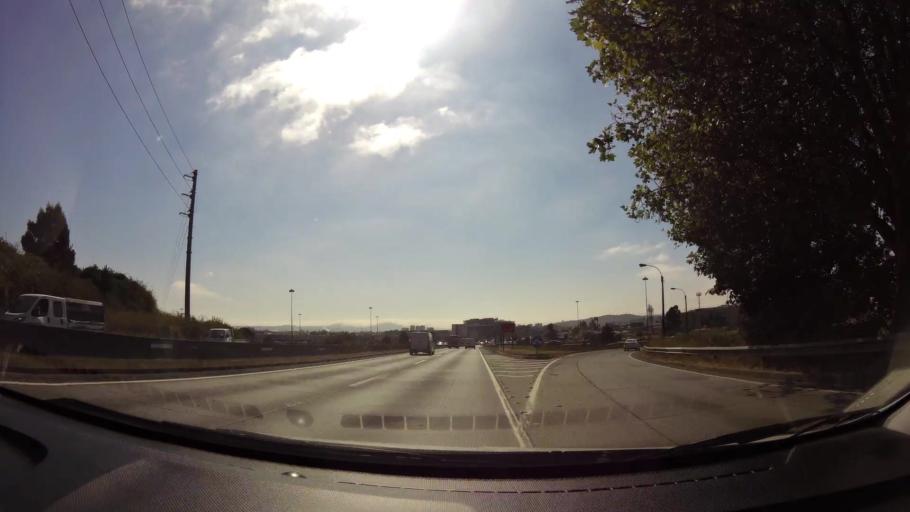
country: CL
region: Biobio
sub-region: Provincia de Concepcion
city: Concepcion
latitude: -36.7962
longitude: -73.0645
